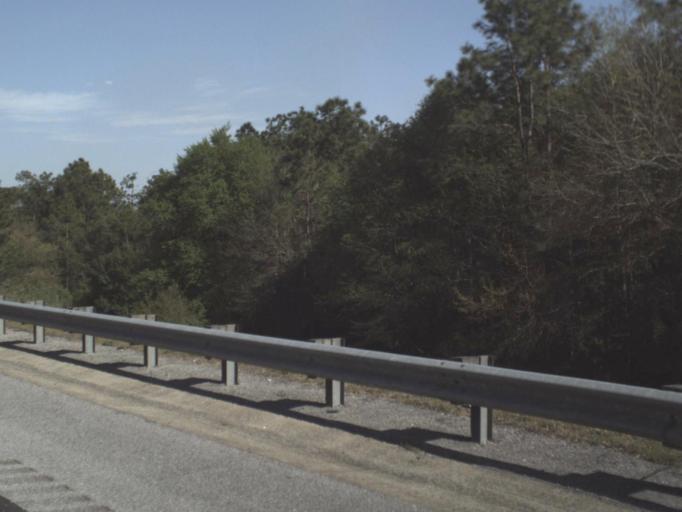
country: US
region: Florida
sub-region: Okaloosa County
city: Crestview
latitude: 30.7157
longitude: -86.6710
